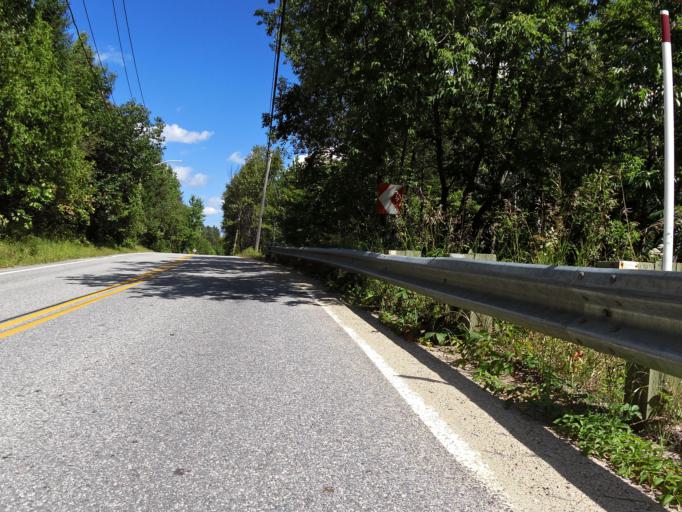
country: CA
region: Quebec
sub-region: Outaouais
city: Maniwaki
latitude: 46.1849
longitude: -76.0499
